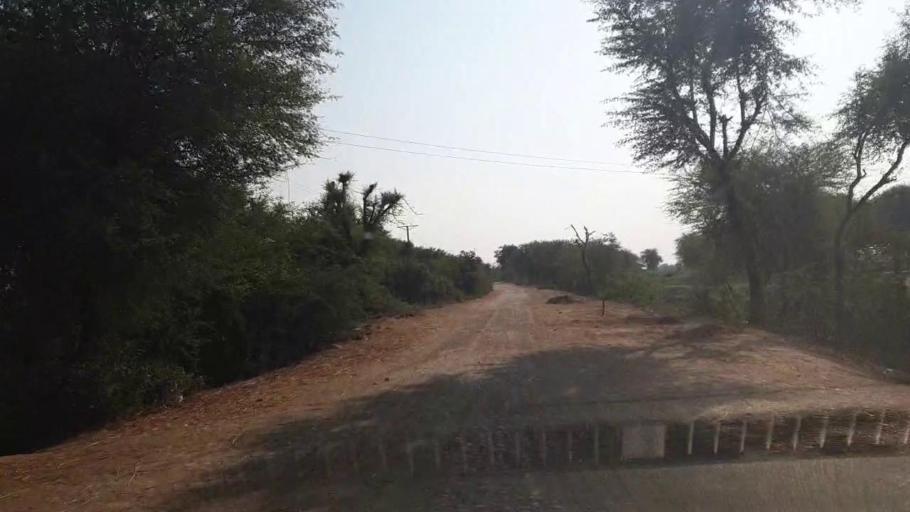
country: PK
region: Sindh
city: Kario
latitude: 24.9010
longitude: 68.6481
